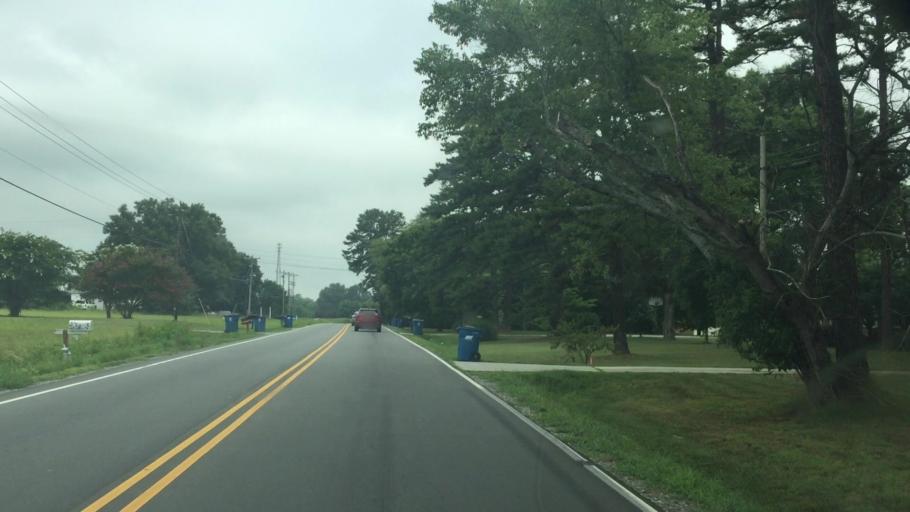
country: US
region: North Carolina
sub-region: Rowan County
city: Enochville
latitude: 35.4427
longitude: -80.7285
